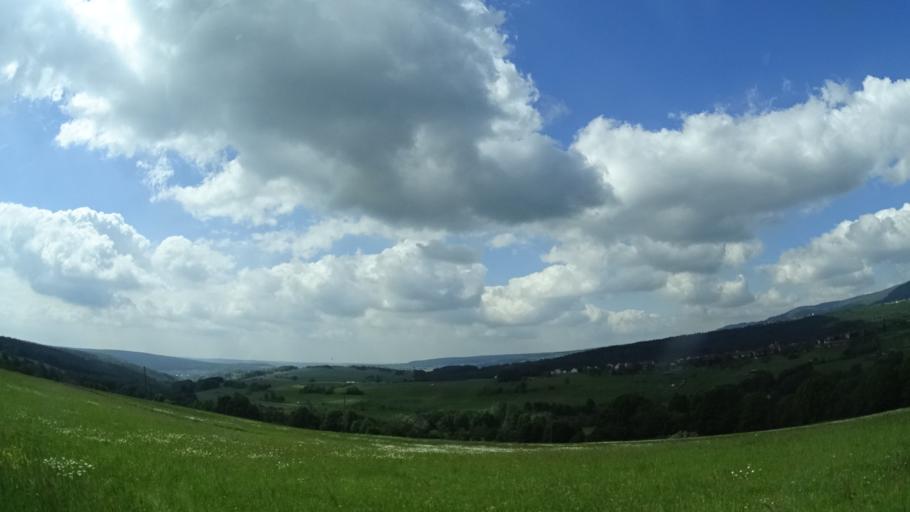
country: DE
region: Bavaria
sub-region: Regierungsbezirk Unterfranken
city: Sandberg
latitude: 50.3430
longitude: 10.0087
